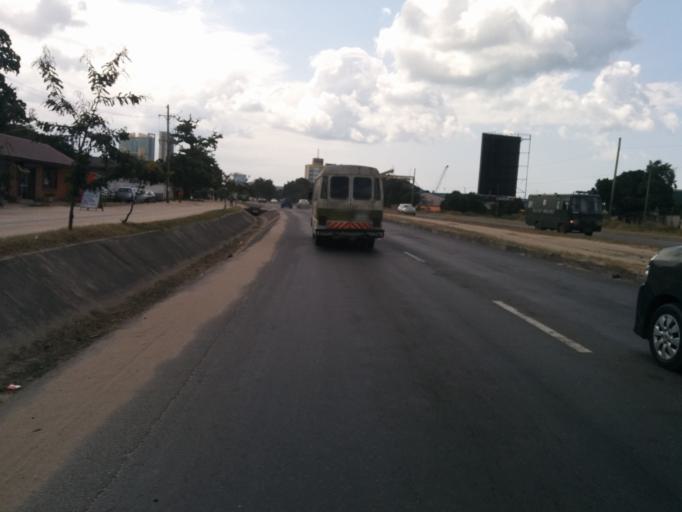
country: TZ
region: Dar es Salaam
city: Dar es Salaam
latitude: -6.8355
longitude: 39.2863
